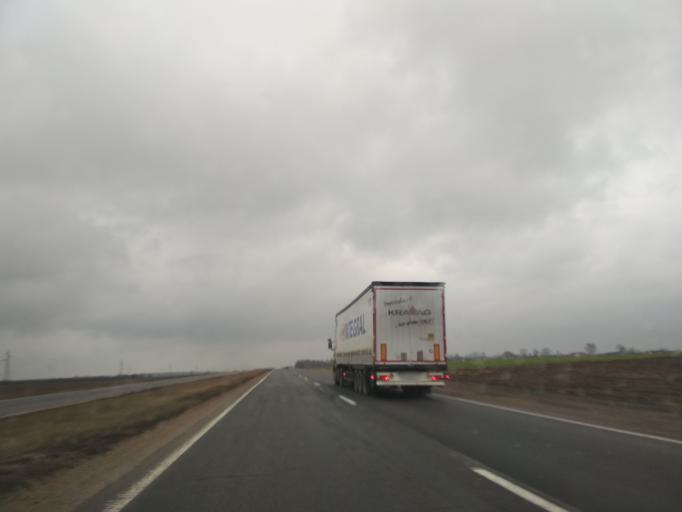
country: BY
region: Minsk
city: Dukora
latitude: 53.6412
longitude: 27.9964
